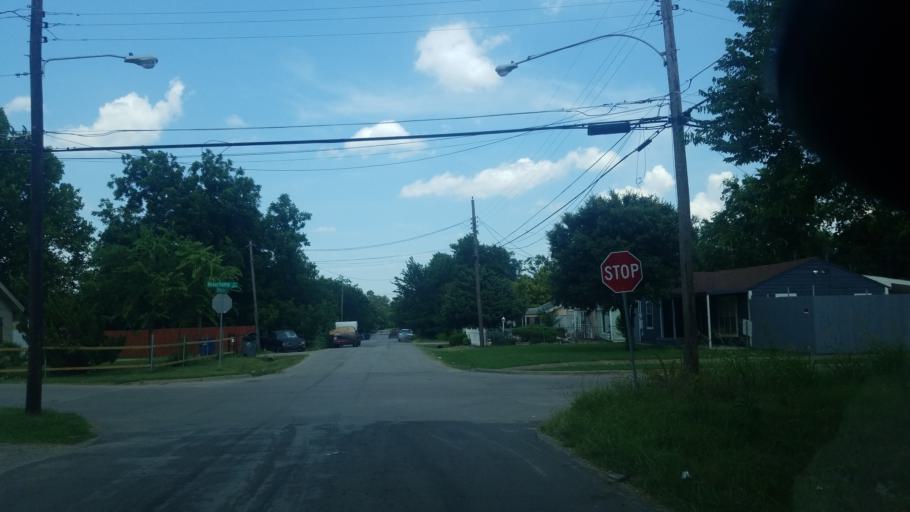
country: US
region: Texas
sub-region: Dallas County
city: Dallas
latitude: 32.7146
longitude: -96.7709
